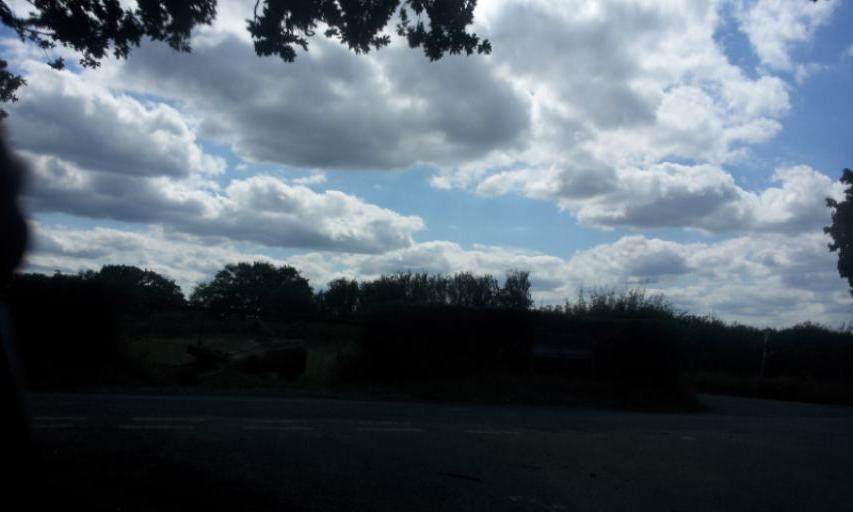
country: GB
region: England
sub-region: Kent
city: Marden
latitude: 51.2117
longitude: 0.5255
